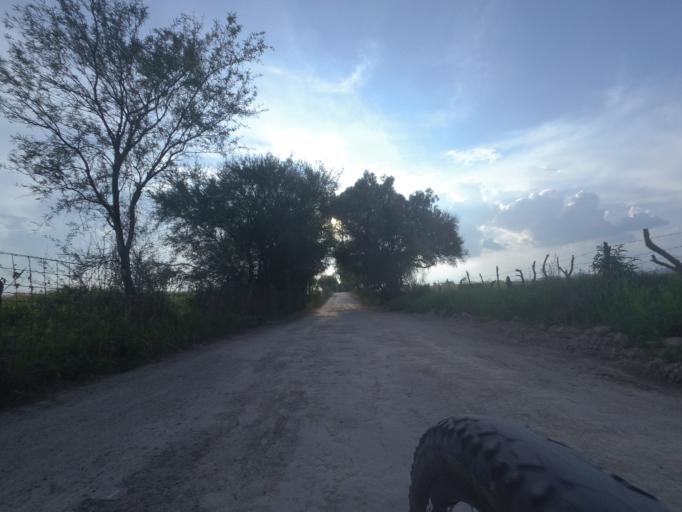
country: MX
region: Aguascalientes
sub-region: Aguascalientes
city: La Loma de los Negritos
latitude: 21.7753
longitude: -102.3659
